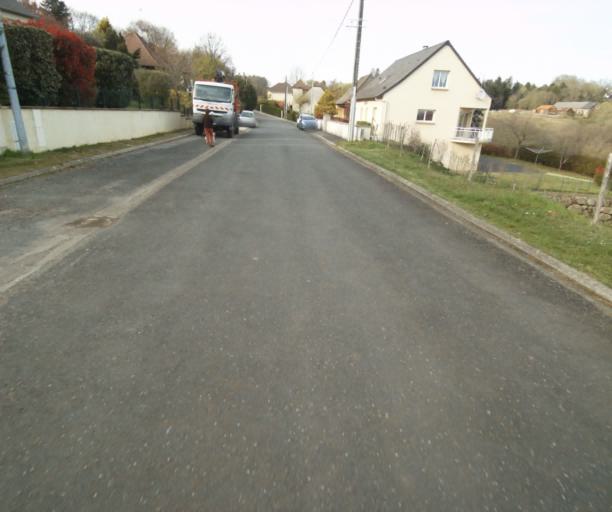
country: FR
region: Limousin
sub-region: Departement de la Correze
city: Naves
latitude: 45.3192
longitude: 1.7661
